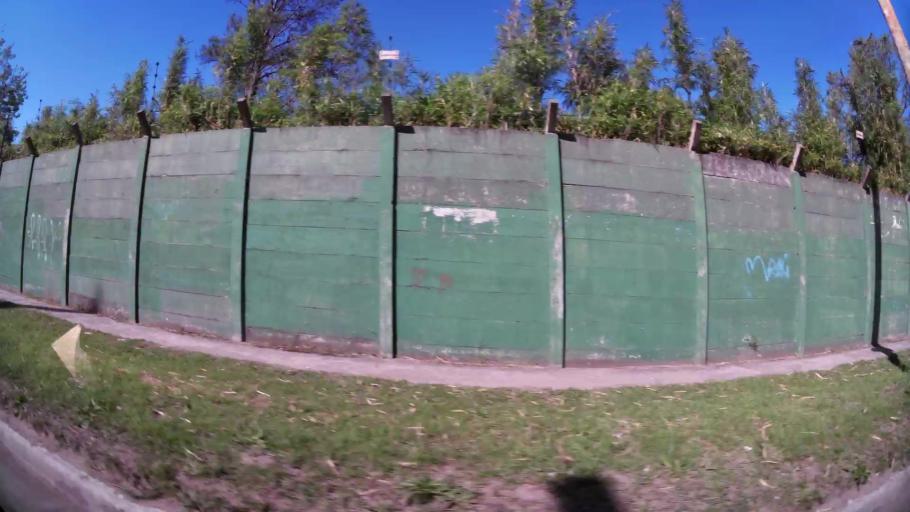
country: AR
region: Buenos Aires
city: Santa Catalina - Dique Lujan
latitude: -34.4700
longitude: -58.7091
